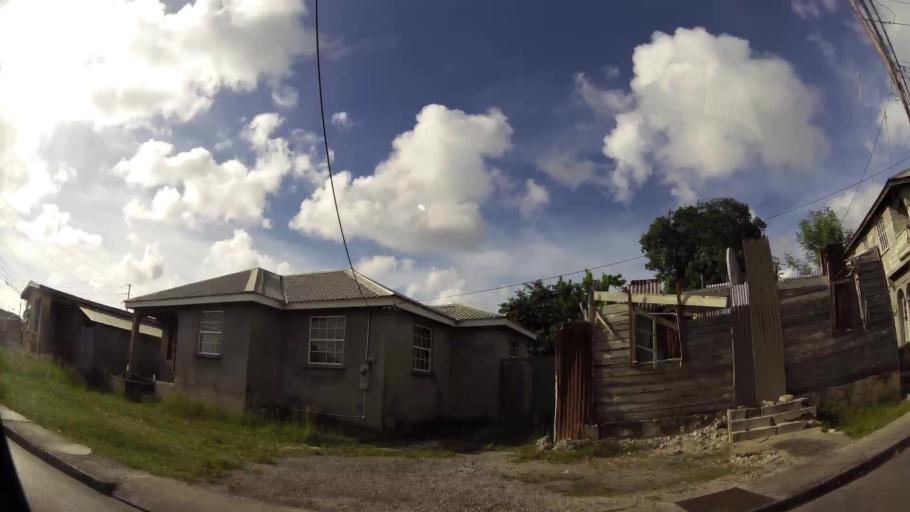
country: BB
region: Saint Michael
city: Bridgetown
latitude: 13.0806
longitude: -59.6006
